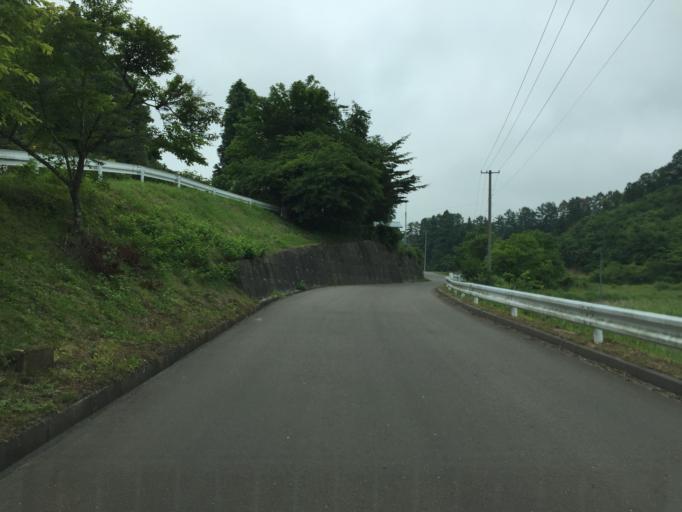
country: JP
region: Miyagi
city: Marumori
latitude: 37.7979
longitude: 140.7444
